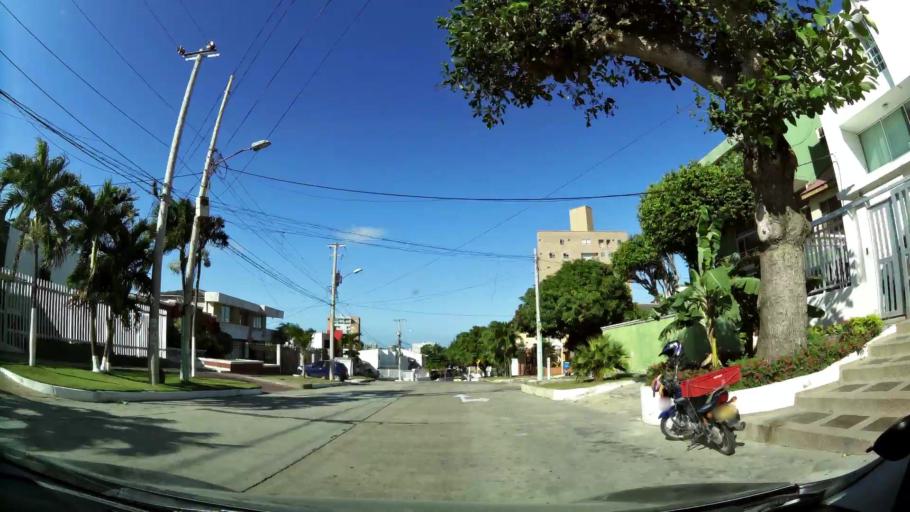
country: CO
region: Atlantico
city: Barranquilla
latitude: 11.0003
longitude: -74.8295
